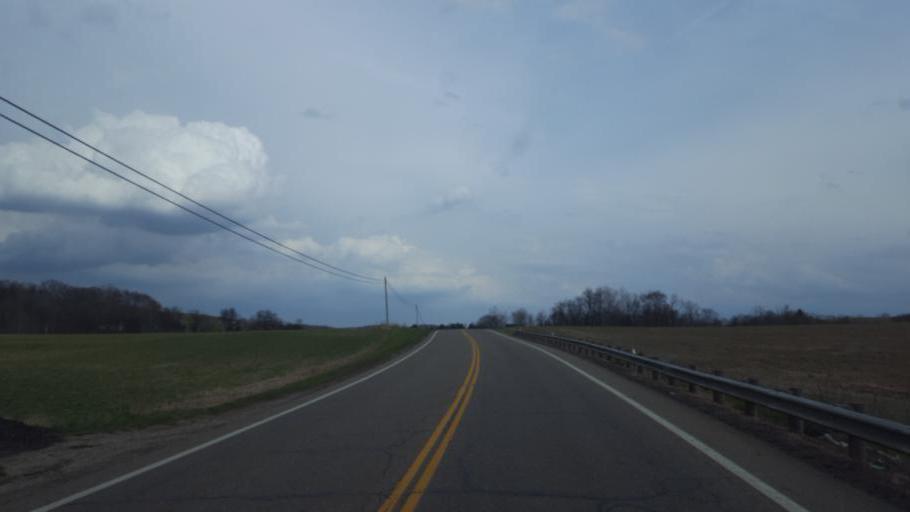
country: US
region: Ohio
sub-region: Coshocton County
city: Coshocton
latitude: 40.2319
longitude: -81.8478
